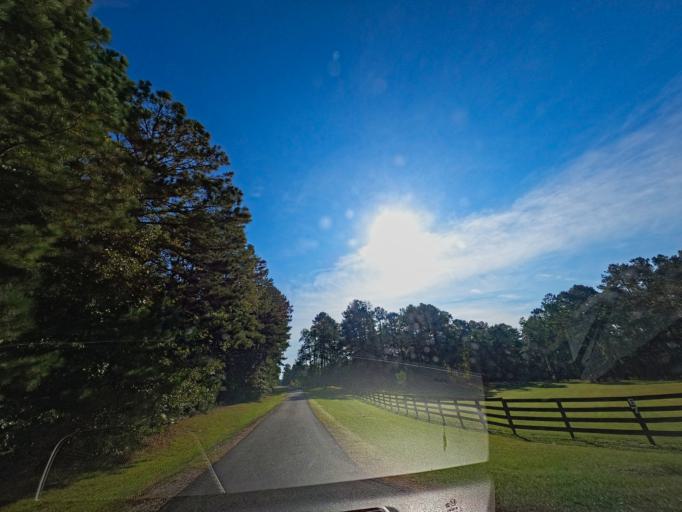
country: US
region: Georgia
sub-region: Coweta County
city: Newnan
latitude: 33.3462
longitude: -84.9149
